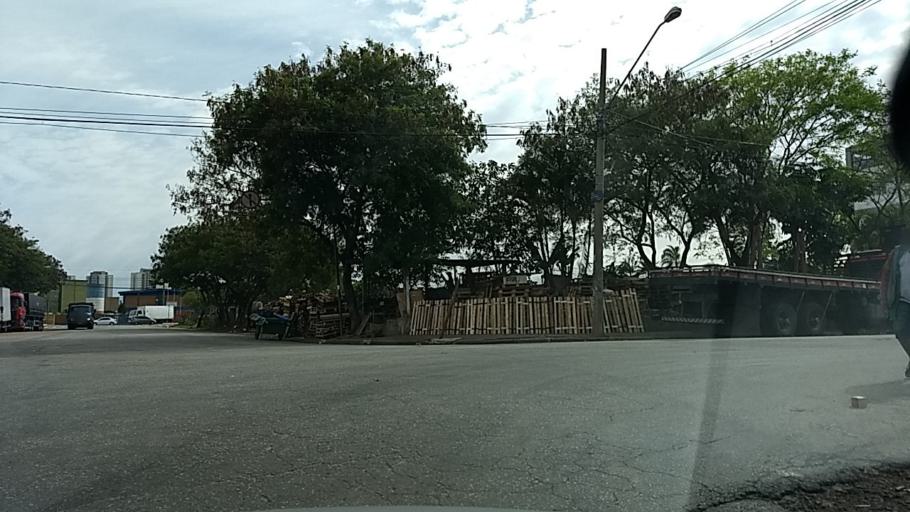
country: BR
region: Sao Paulo
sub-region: Guarulhos
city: Guarulhos
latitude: -23.4918
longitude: -46.5666
